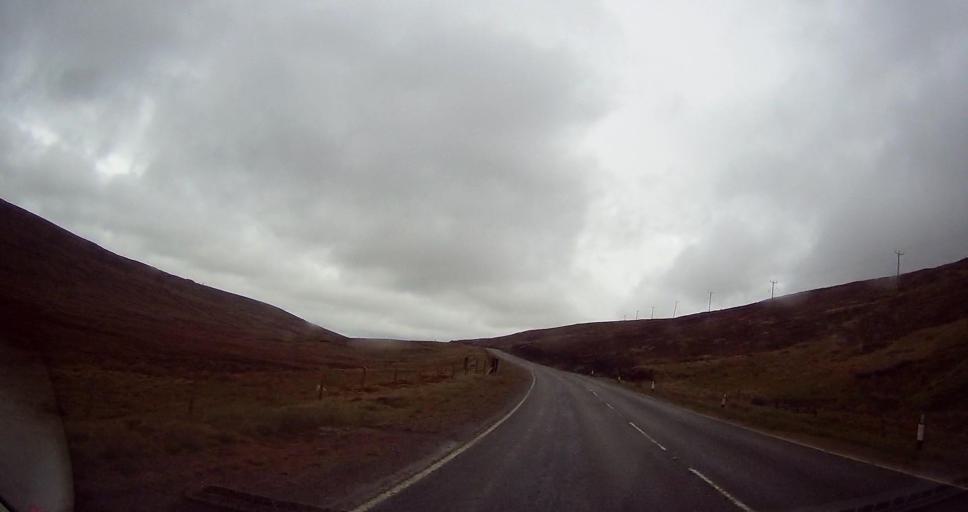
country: GB
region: Scotland
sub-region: Shetland Islands
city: Lerwick
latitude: 60.3172
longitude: -1.2469
